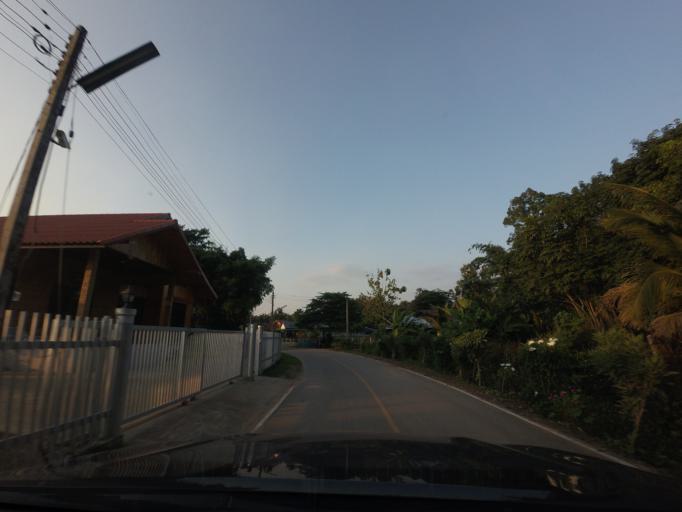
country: TH
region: Nan
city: Na Noi
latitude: 18.3123
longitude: 100.7334
